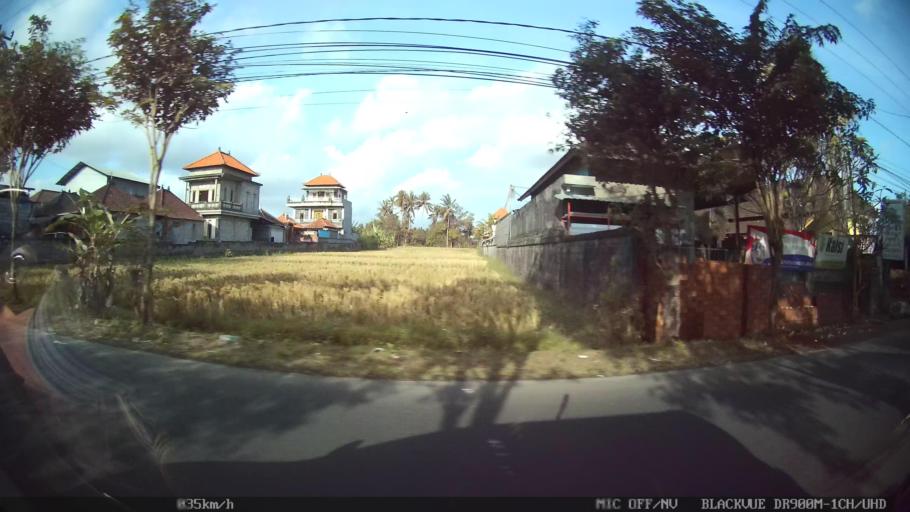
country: ID
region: Bali
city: Banjar Sedang
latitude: -8.5663
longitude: 115.2344
